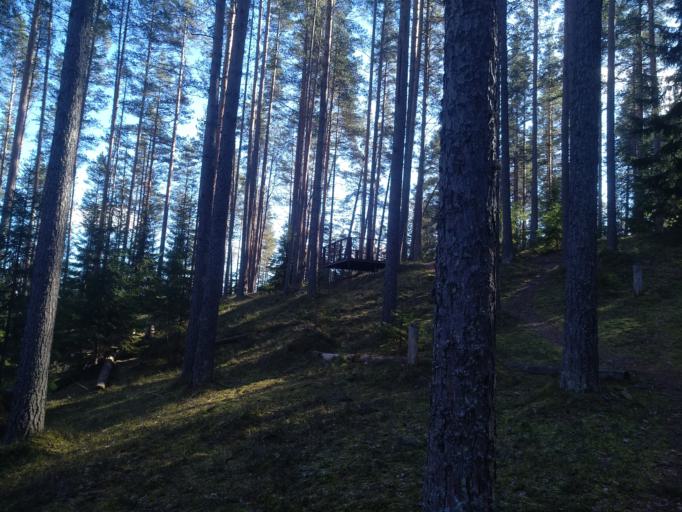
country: RU
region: Leningrad
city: Sapernoye
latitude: 60.6257
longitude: 30.0707
